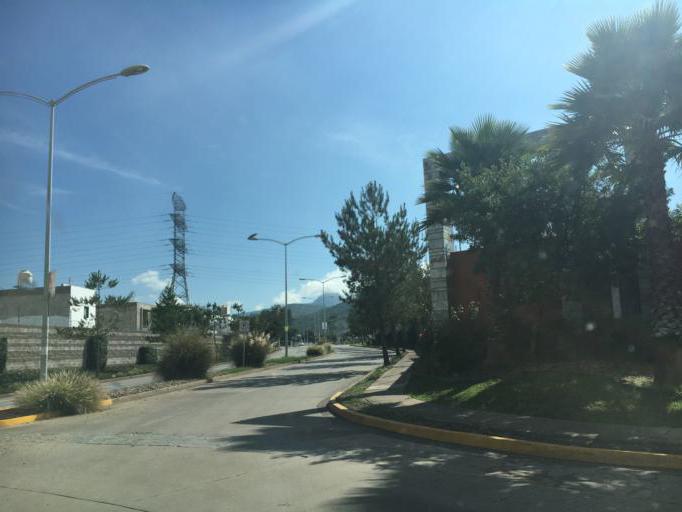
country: MX
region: Guanajuato
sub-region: Leon
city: Medina
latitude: 21.1329
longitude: -101.6150
